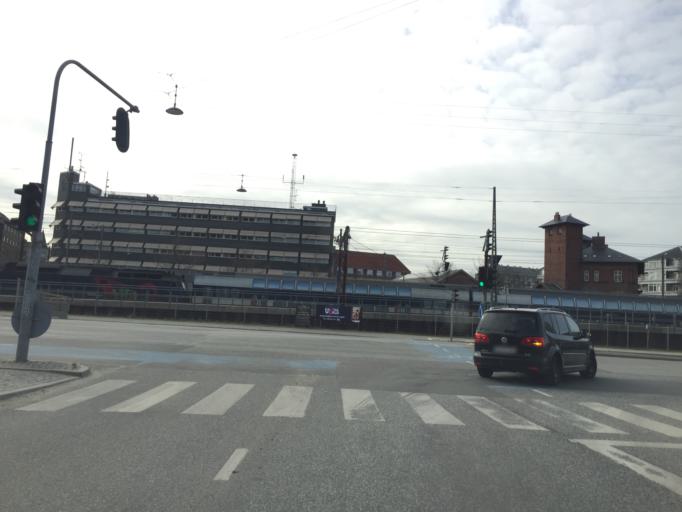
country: DK
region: Capital Region
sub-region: Kobenhavn
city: Christianshavn
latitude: 55.7011
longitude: 12.5929
